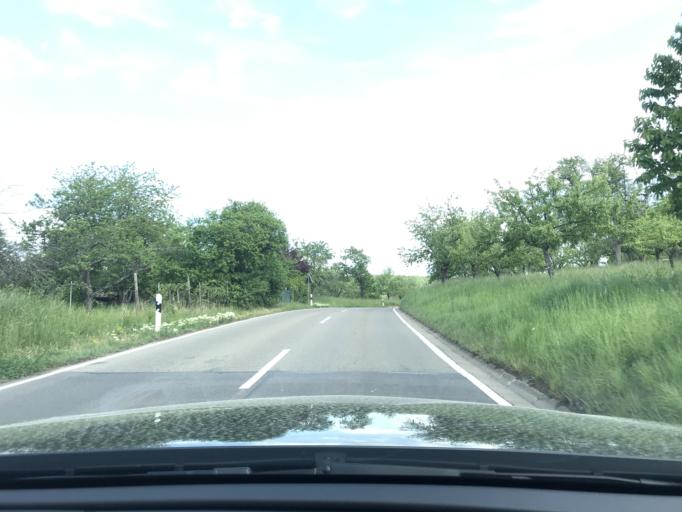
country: DE
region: Baden-Wuerttemberg
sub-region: Regierungsbezirk Stuttgart
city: Weinstadt-Endersbach
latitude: 48.7756
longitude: 9.3684
